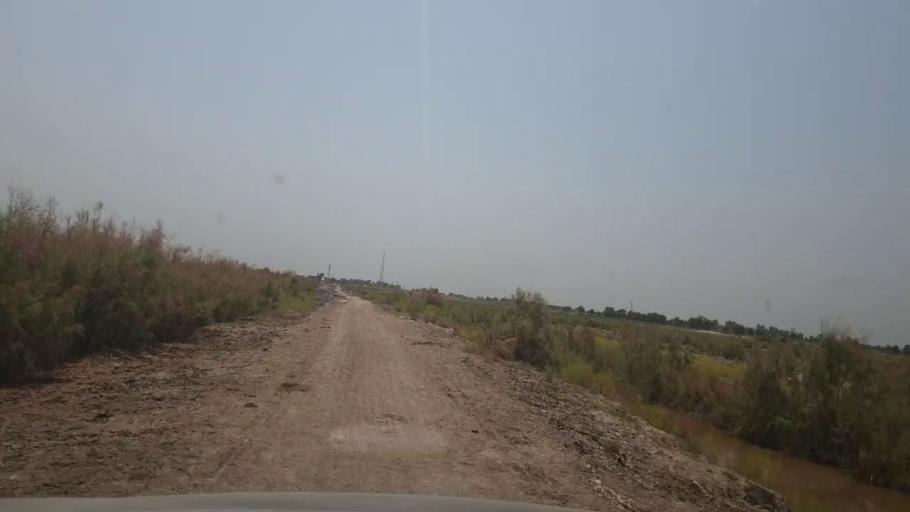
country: PK
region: Sindh
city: Lakhi
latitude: 27.8335
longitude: 68.6588
